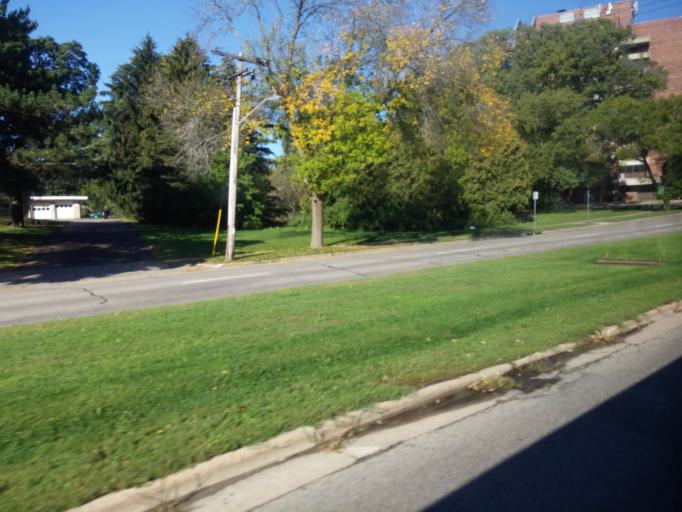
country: US
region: Wisconsin
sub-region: Dane County
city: Shorewood Hills
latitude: 43.0715
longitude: -89.4552
